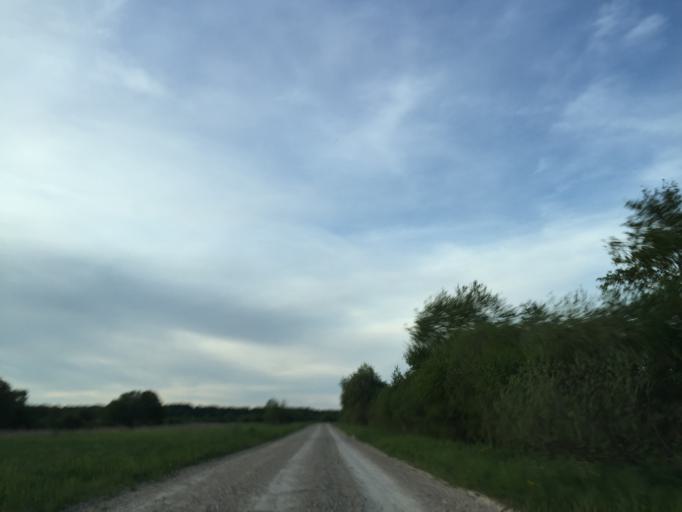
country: LV
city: Tireli
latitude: 56.7700
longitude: 23.5429
